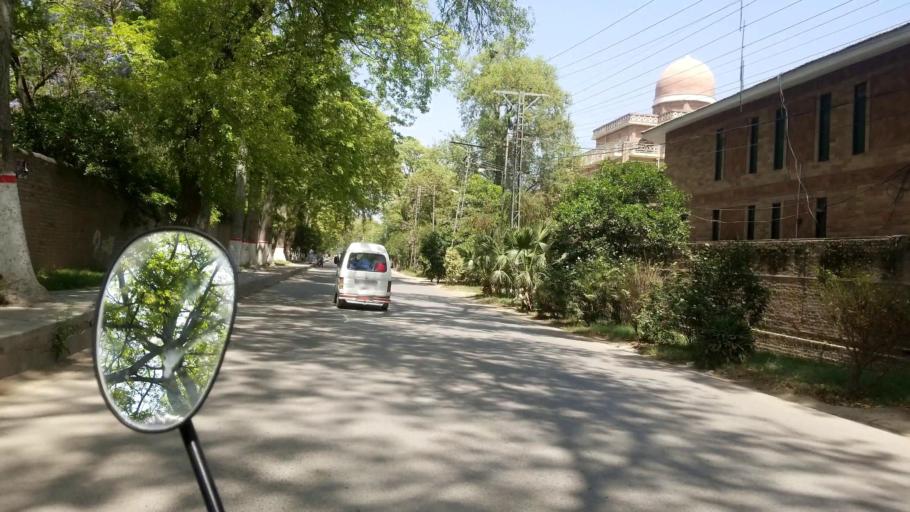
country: PK
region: Khyber Pakhtunkhwa
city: Peshawar
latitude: 34.0076
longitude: 71.4866
